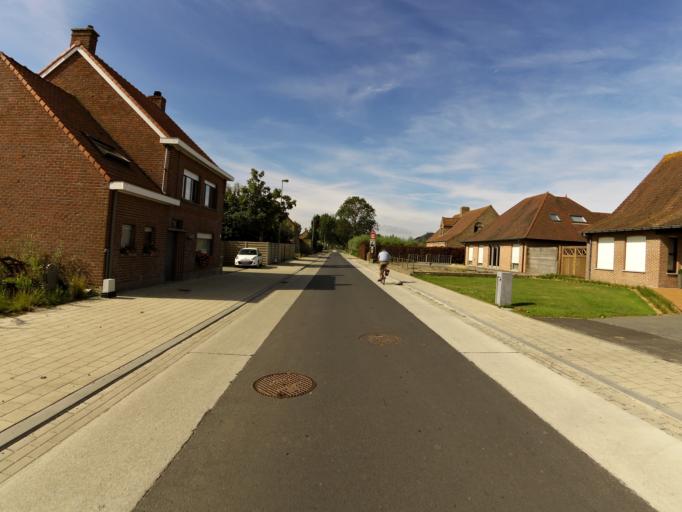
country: BE
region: Flanders
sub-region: Provincie West-Vlaanderen
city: Houthulst
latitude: 51.0292
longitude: 2.9558
